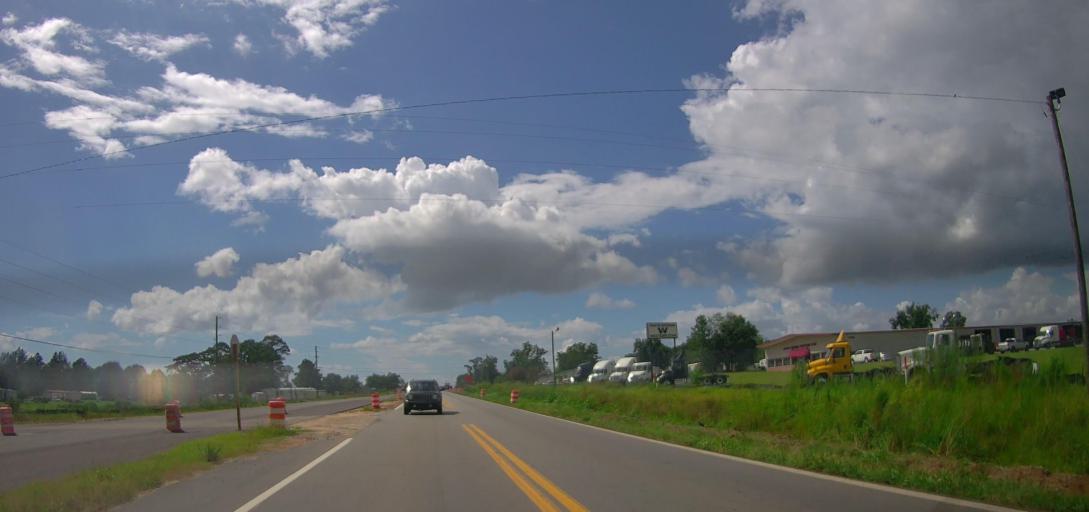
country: US
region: Georgia
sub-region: Coffee County
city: Douglas
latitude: 31.5351
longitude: -82.9180
